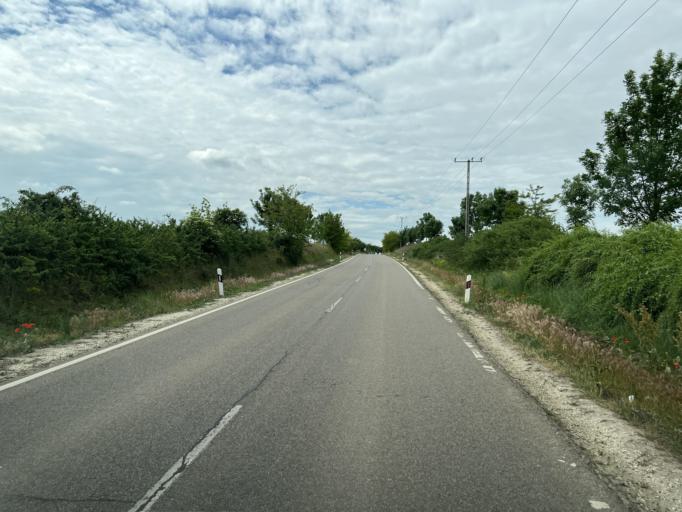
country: HU
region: Pest
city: Koka
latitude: 47.5040
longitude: 19.5924
